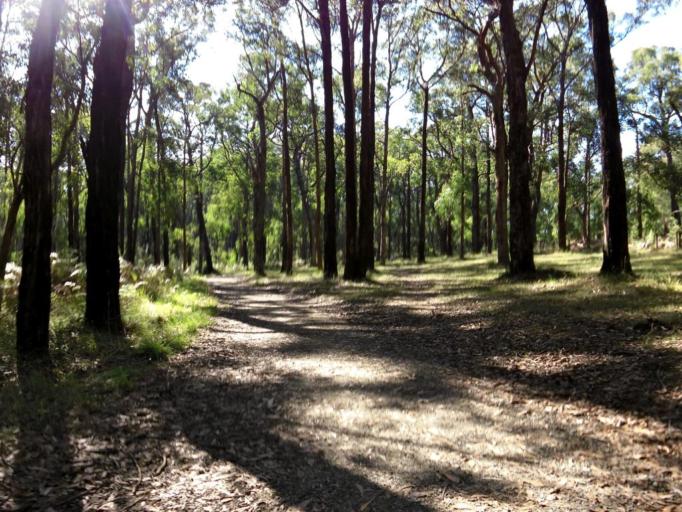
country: AU
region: Victoria
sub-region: Cardinia
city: Cockatoo
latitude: -37.9312
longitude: 145.4821
